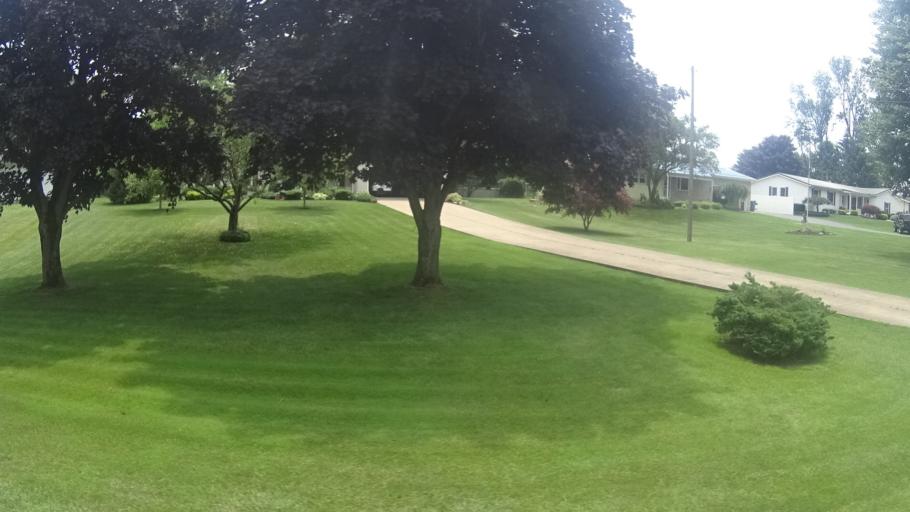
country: US
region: Ohio
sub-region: Erie County
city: Milan
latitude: 41.3070
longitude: -82.6154
